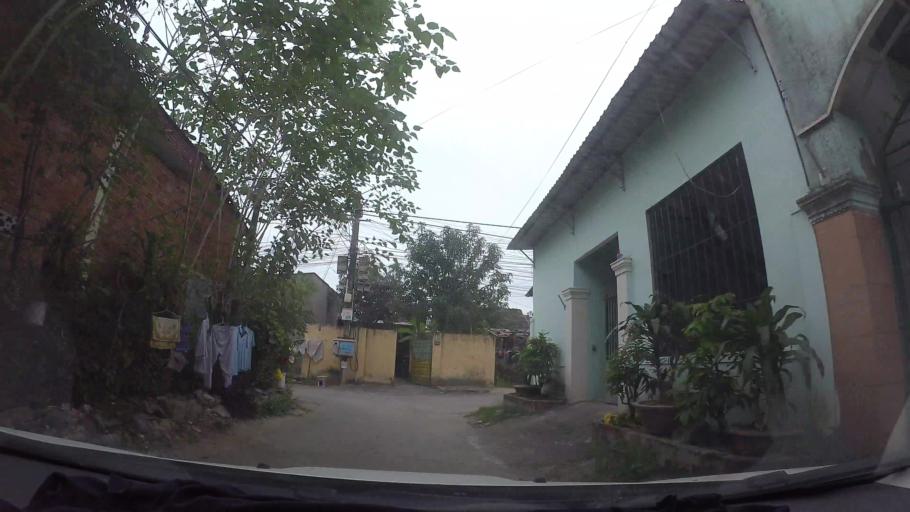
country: VN
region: Da Nang
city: Lien Chieu
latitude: 16.0675
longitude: 108.1428
